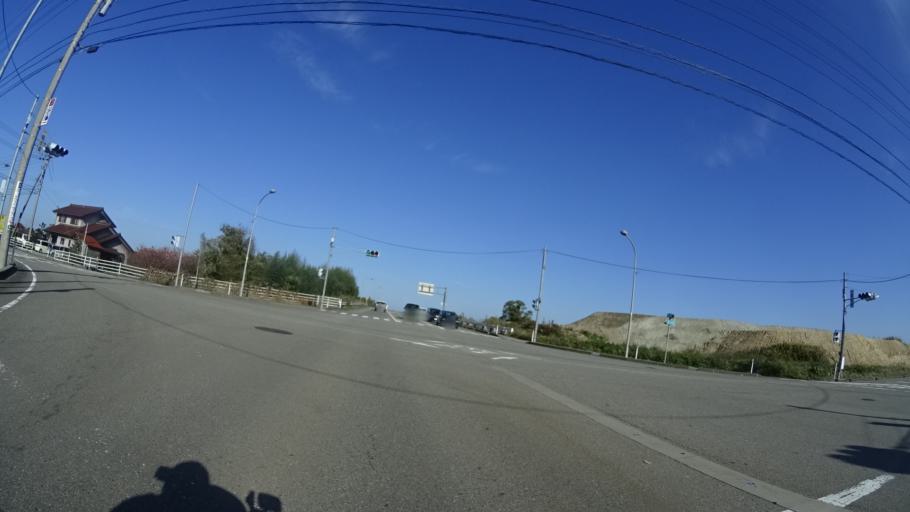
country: JP
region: Ishikawa
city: Komatsu
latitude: 36.3015
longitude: 136.3867
